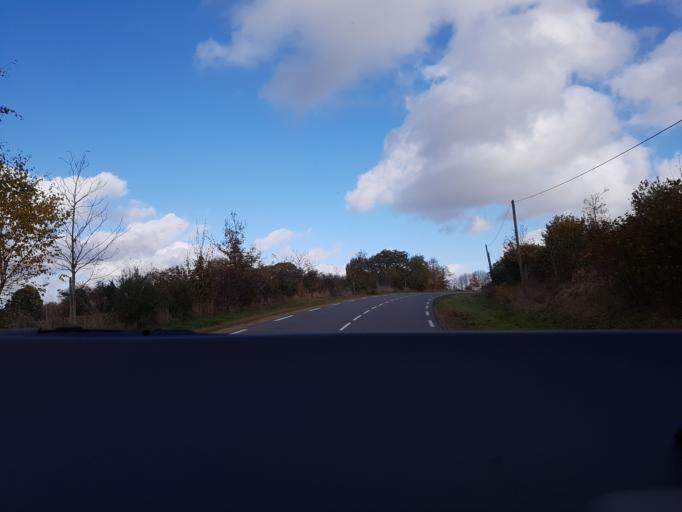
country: FR
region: Lower Normandy
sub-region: Departement de l'Orne
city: Champsecret
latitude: 48.6396
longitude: -0.5500
